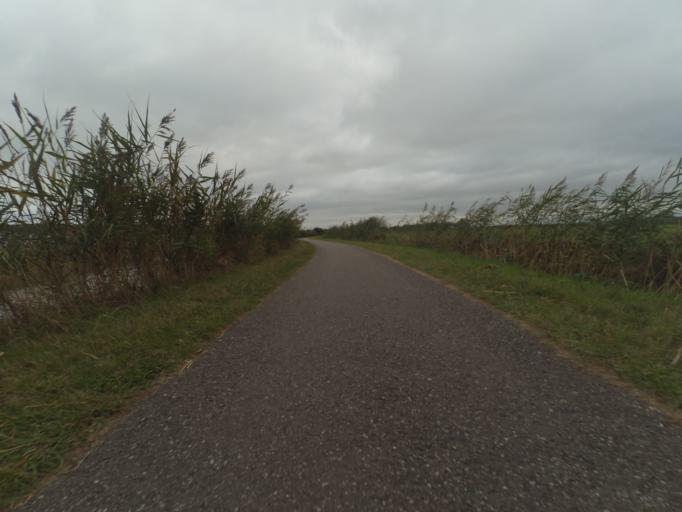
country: NL
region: Utrecht
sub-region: Gemeente Rhenen
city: Rhenen
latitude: 51.9919
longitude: 5.6114
